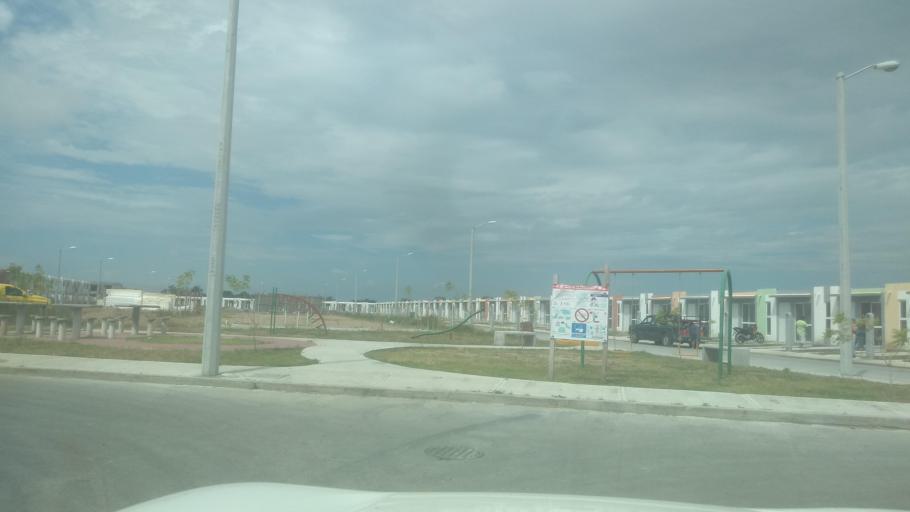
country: MX
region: Veracruz
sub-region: Medellin
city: Fraccionamiento Arboledas San Ramon
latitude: 19.0997
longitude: -96.1676
